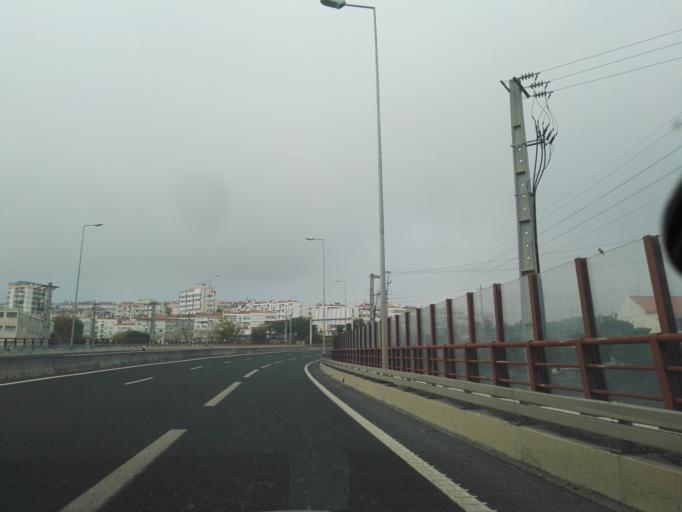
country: PT
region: Lisbon
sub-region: Loures
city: Santa Iria da Azoia
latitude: 38.8461
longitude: -9.0798
